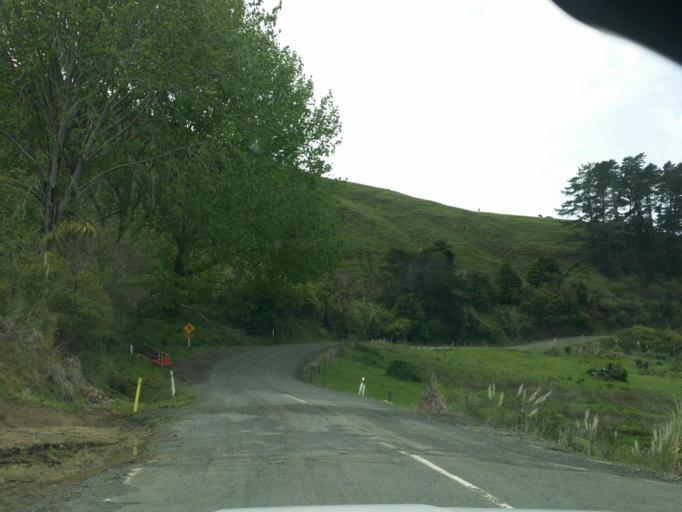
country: NZ
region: Northland
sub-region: Whangarei
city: Maungatapere
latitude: -35.8984
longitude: 174.0935
